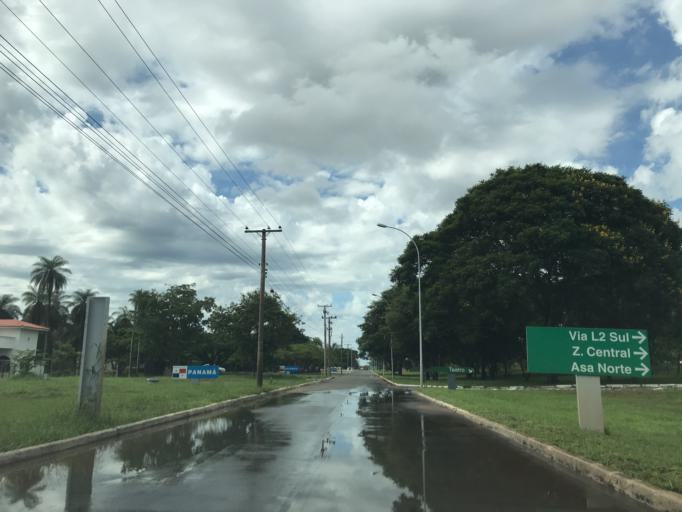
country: BR
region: Federal District
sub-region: Brasilia
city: Brasilia
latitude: -15.8085
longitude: -47.8788
